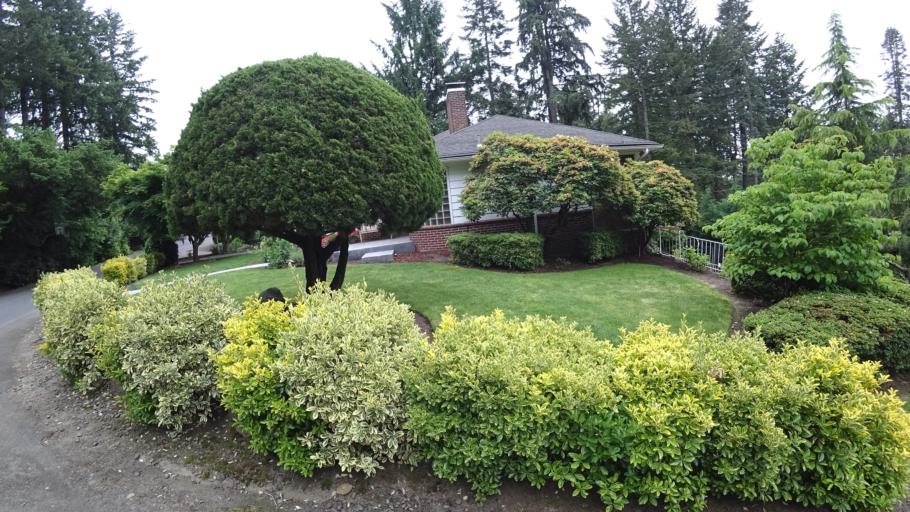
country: US
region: Oregon
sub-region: Multnomah County
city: Portland
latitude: 45.4847
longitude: -122.6970
